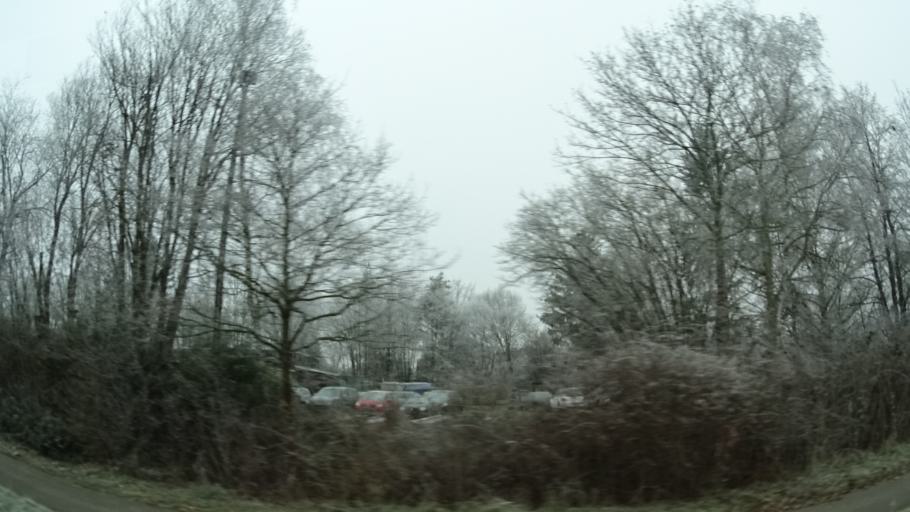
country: DE
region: Bavaria
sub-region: Regierungsbezirk Unterfranken
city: Hassfurt
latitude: 50.0435
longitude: 10.5199
